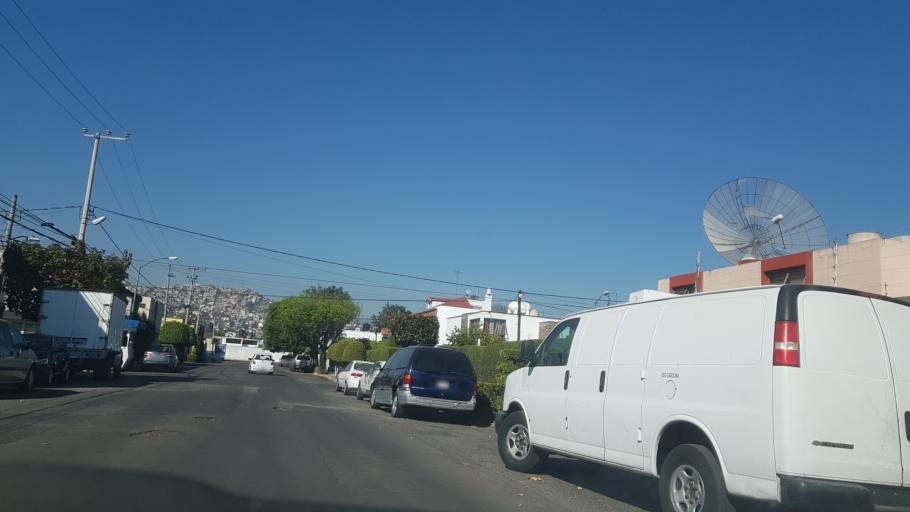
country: MX
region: Mexico
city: Naucalpan de Juarez
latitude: 19.4922
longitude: -99.2492
